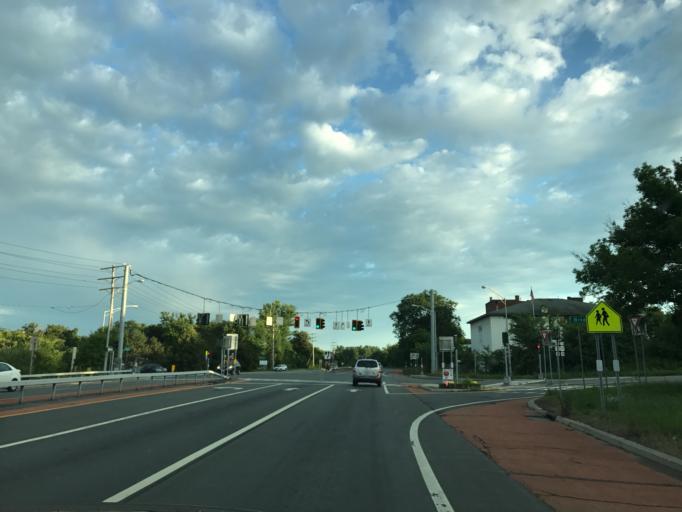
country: US
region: New York
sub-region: Albany County
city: Cohoes
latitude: 42.7697
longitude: -73.6978
